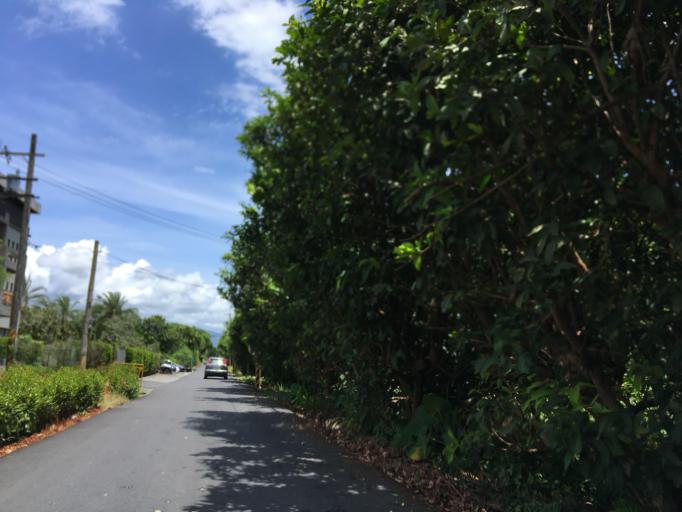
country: TW
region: Taiwan
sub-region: Yilan
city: Yilan
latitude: 24.6382
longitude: 121.7203
